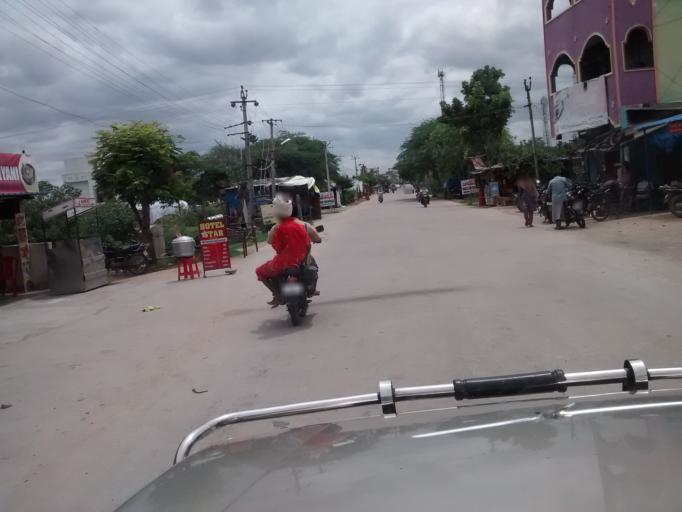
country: IN
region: Andhra Pradesh
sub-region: Chittoor
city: Chittoor
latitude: 13.2770
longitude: 79.0416
